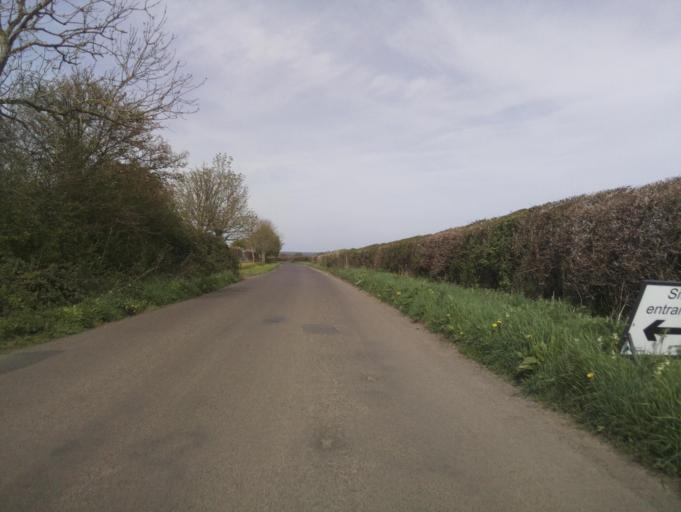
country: GB
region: England
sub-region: Somerset
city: Ilchester
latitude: 51.0192
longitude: -2.6363
